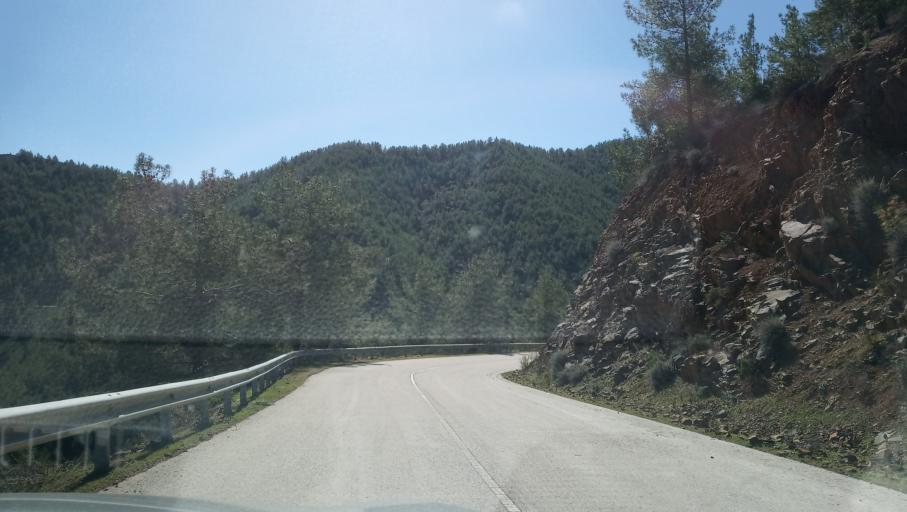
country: CY
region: Lefkosia
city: Lefka
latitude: 35.0717
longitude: 32.7545
